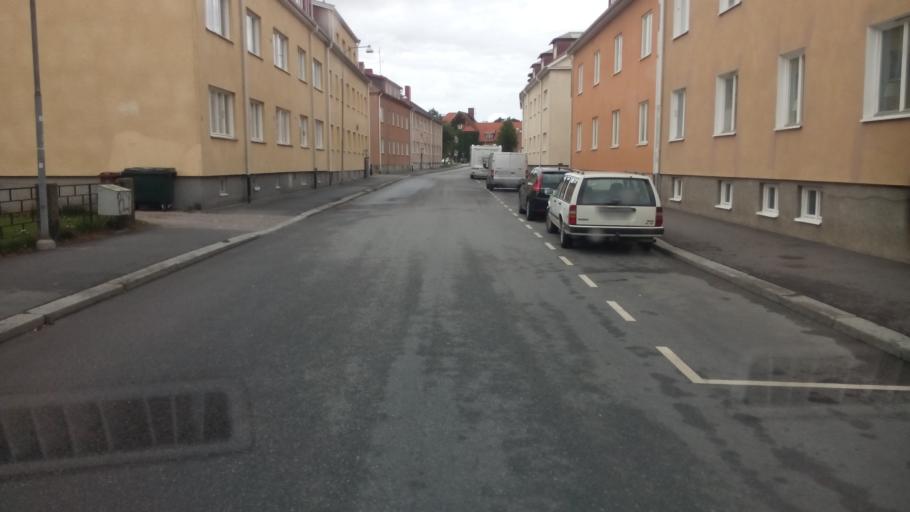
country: SE
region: Soedermanland
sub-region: Nykopings Kommun
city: Nykoping
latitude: 58.7550
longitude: 16.9980
